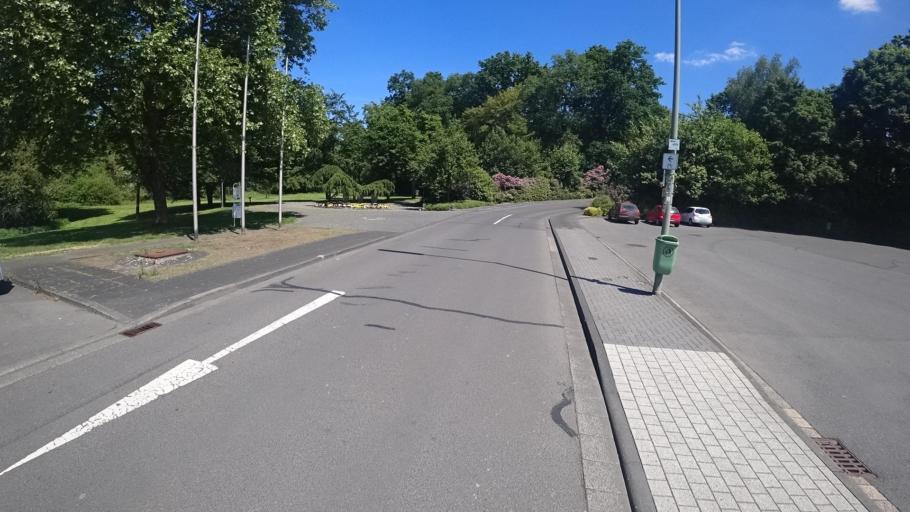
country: DE
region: Rheinland-Pfalz
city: Altenkirchen
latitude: 50.6899
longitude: 7.6463
